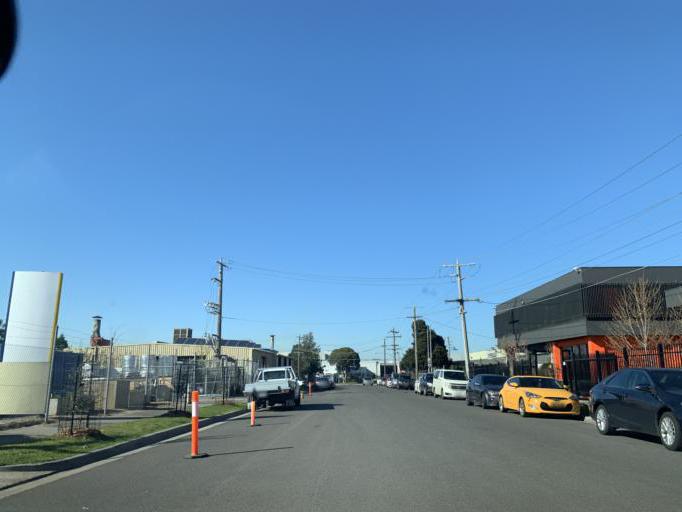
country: AU
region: Victoria
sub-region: Greater Dandenong
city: Dandenong
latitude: -37.9853
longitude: 145.1893
